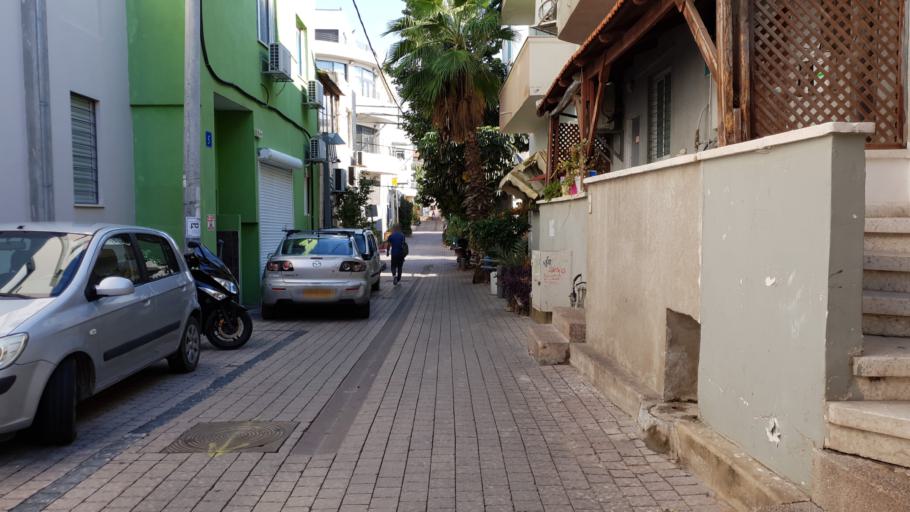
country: IL
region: Tel Aviv
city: Tel Aviv
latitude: 32.0702
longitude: 34.7669
